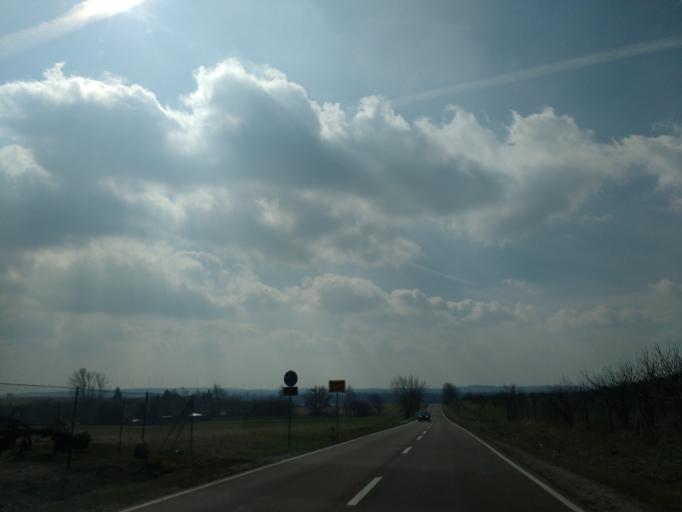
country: DE
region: Saxony-Anhalt
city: Roblingen am See
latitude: 51.4860
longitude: 11.6748
